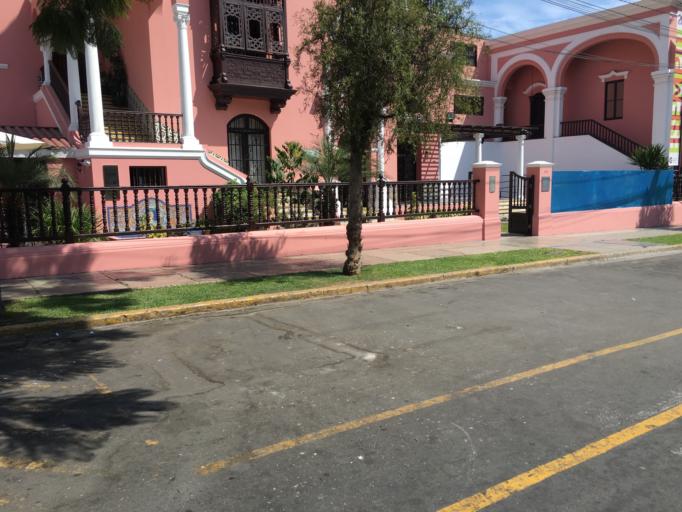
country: PE
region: Lima
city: Lima
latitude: -12.0703
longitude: -77.0373
